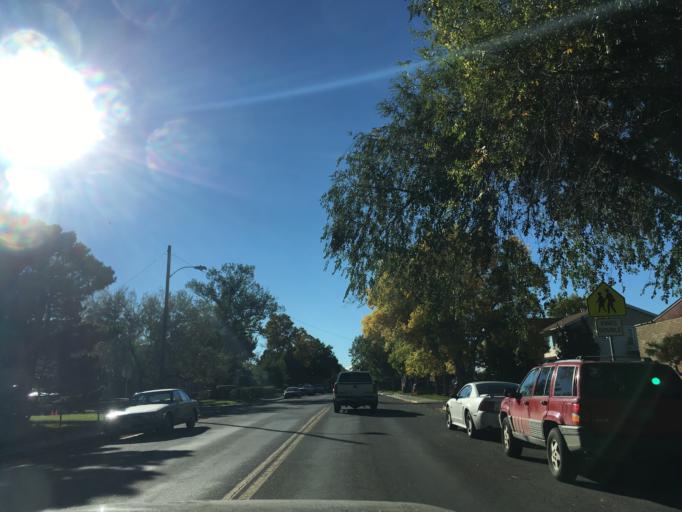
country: US
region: Montana
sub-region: Yellowstone County
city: Billings
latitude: 45.7899
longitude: -108.5325
